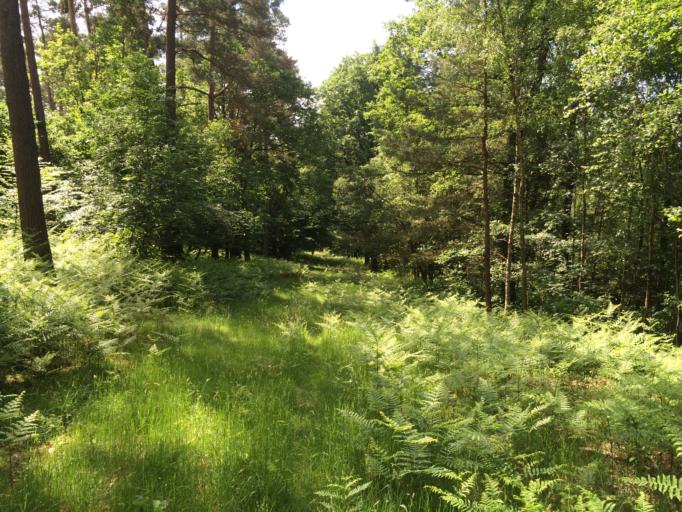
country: BE
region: Wallonia
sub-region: Province de Namur
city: Yvoir
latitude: 50.3362
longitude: 4.9506
